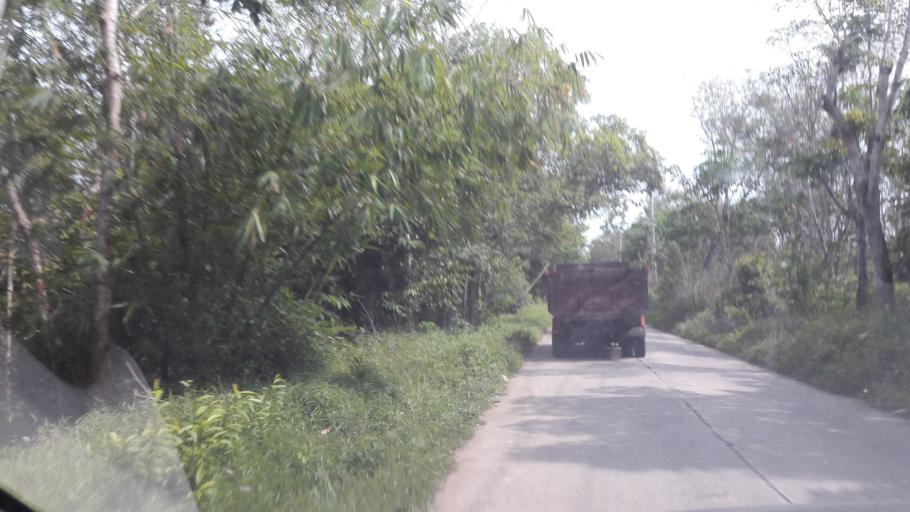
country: ID
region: South Sumatra
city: Gunungmenang
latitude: -3.2459
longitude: 104.1354
